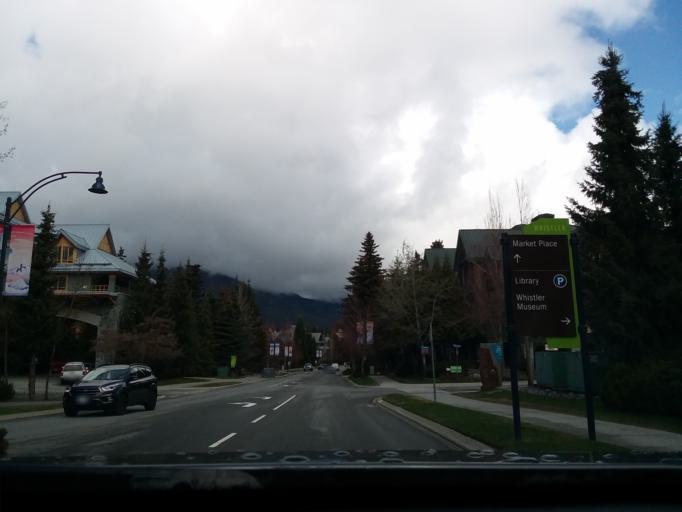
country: CA
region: British Columbia
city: Whistler
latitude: 50.1167
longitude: -122.9575
